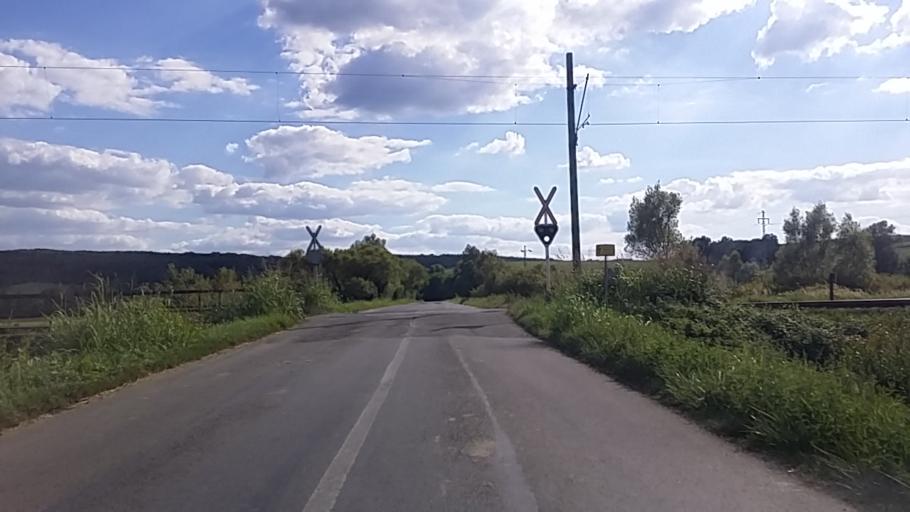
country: HU
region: Baranya
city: Sasd
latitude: 46.2170
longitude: 18.1070
